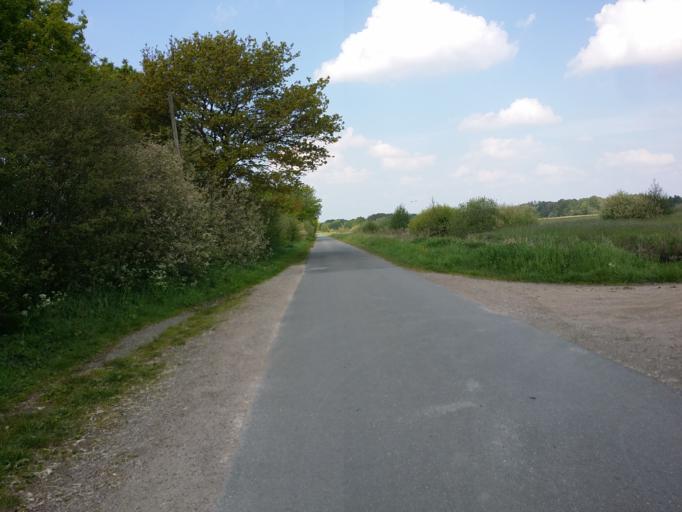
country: DE
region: Lower Saxony
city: Osterholz-Scharmbeck
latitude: 53.2242
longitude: 8.8412
